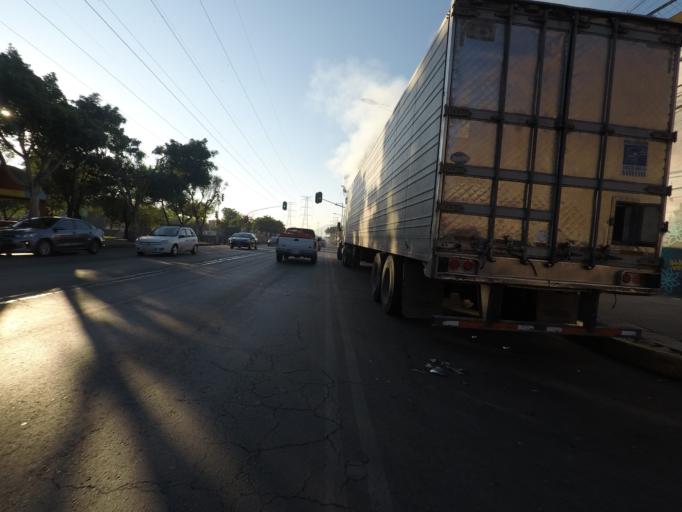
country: MX
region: Mexico City
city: Iztapalapa
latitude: 19.3697
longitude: -99.0774
